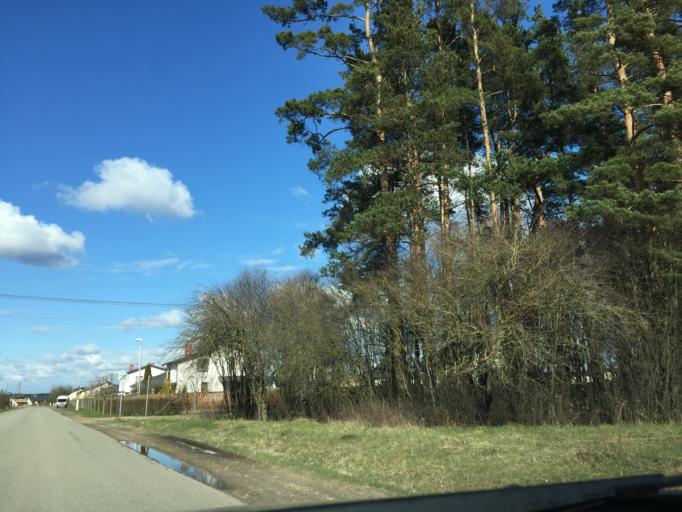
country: LV
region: Kekava
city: Kekava
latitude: 56.8359
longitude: 24.2069
